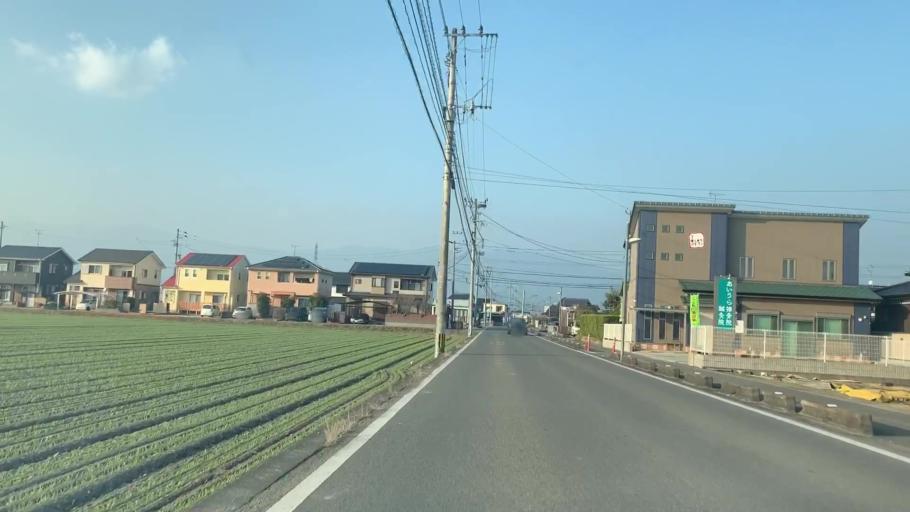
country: JP
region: Saga Prefecture
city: Saga-shi
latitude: 33.2639
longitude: 130.2313
